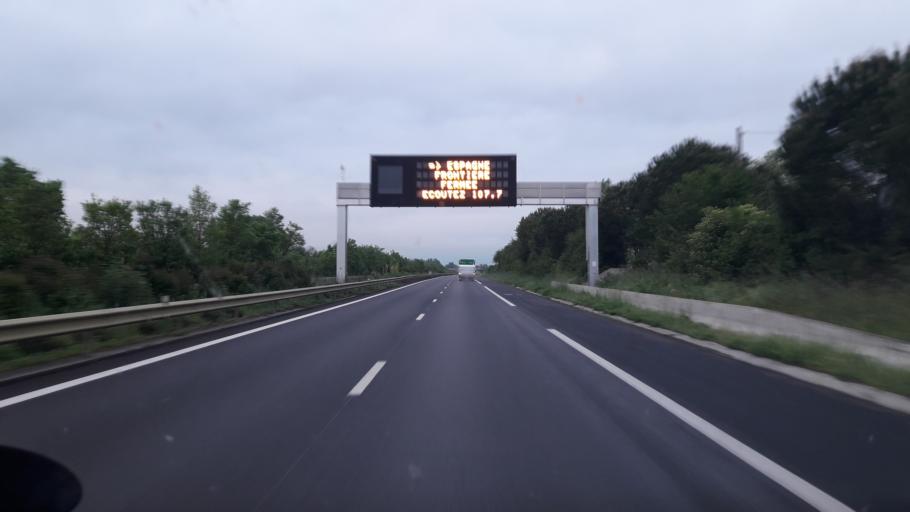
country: FR
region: Midi-Pyrenees
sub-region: Departement de la Haute-Garonne
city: Le Fauga
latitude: 43.3933
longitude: 1.2866
